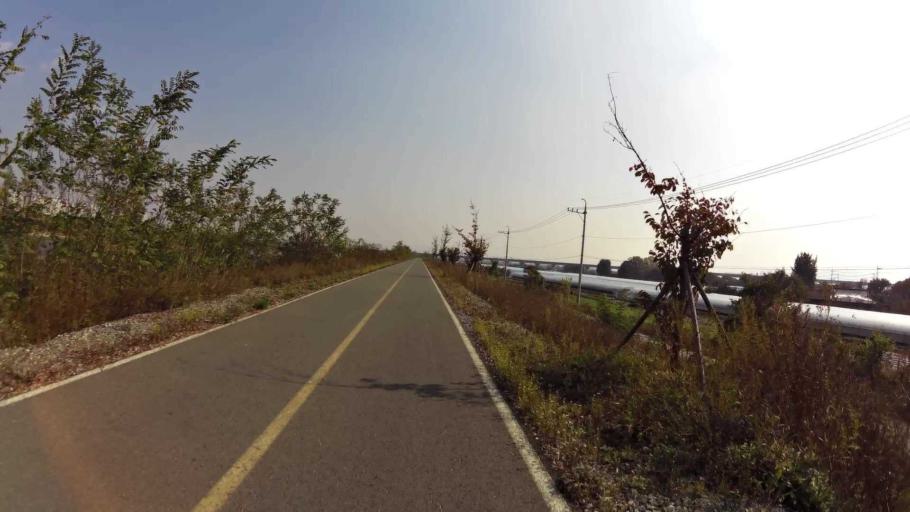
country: KR
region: Gyeongsangbuk-do
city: Gyeongsan-si
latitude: 35.8602
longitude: 128.7182
